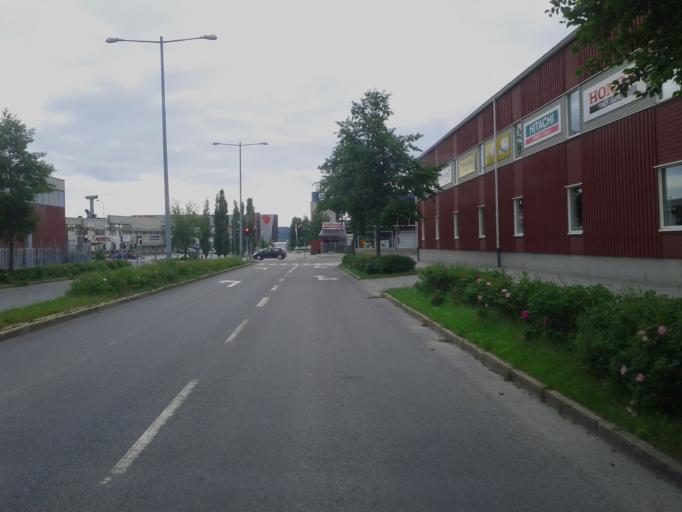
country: SE
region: Vaesternorrland
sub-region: OErnskoeldsviks Kommun
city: Ornskoldsvik
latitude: 63.2879
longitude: 18.7211
